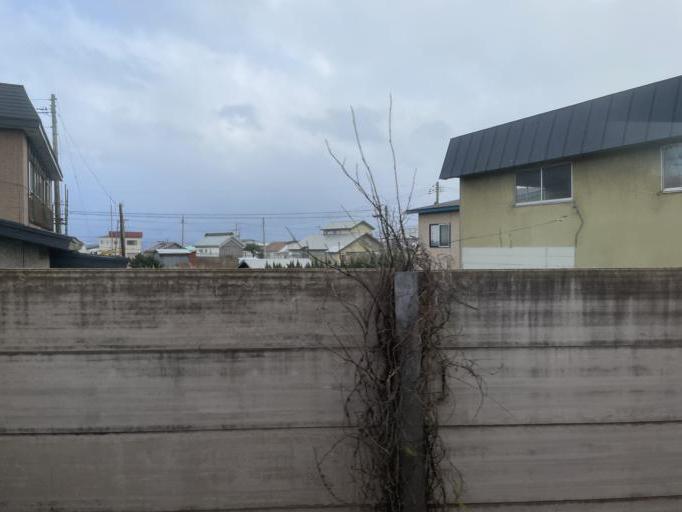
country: JP
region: Aomori
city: Aomori Shi
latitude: 41.0180
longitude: 140.6467
